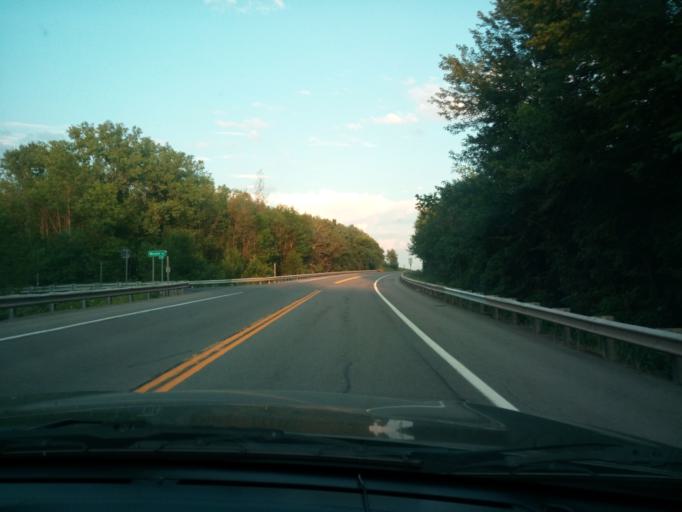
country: US
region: New York
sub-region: Wayne County
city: Clyde
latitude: 43.0724
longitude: -76.7788
